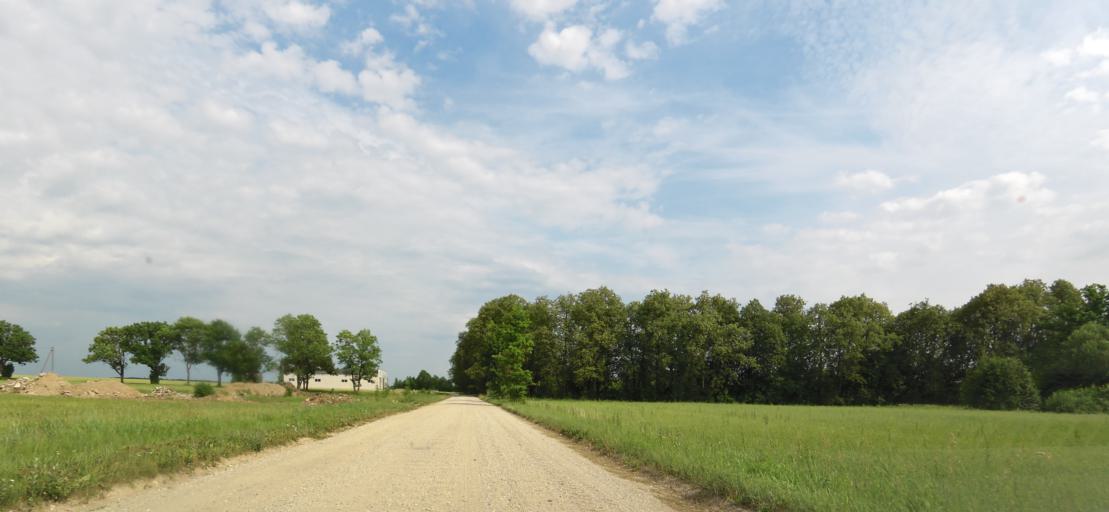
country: LT
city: Obeliai
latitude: 56.1526
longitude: 25.0389
